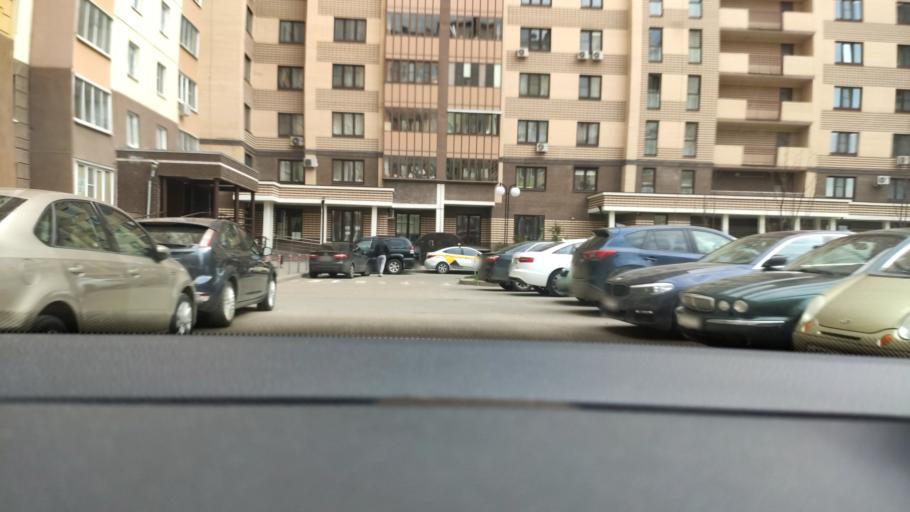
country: RU
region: Moskovskaya
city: Lesnoy Gorodok
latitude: 55.6567
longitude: 37.2275
